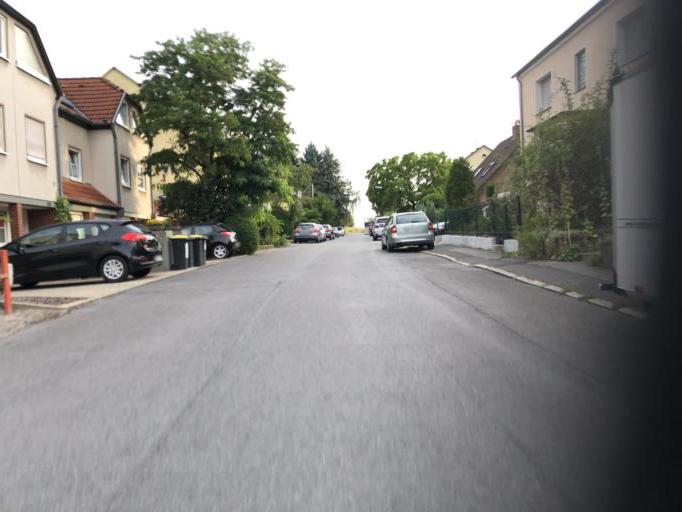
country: DE
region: North Rhine-Westphalia
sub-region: Regierungsbezirk Arnsberg
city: Dortmund
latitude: 51.4914
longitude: 7.4214
